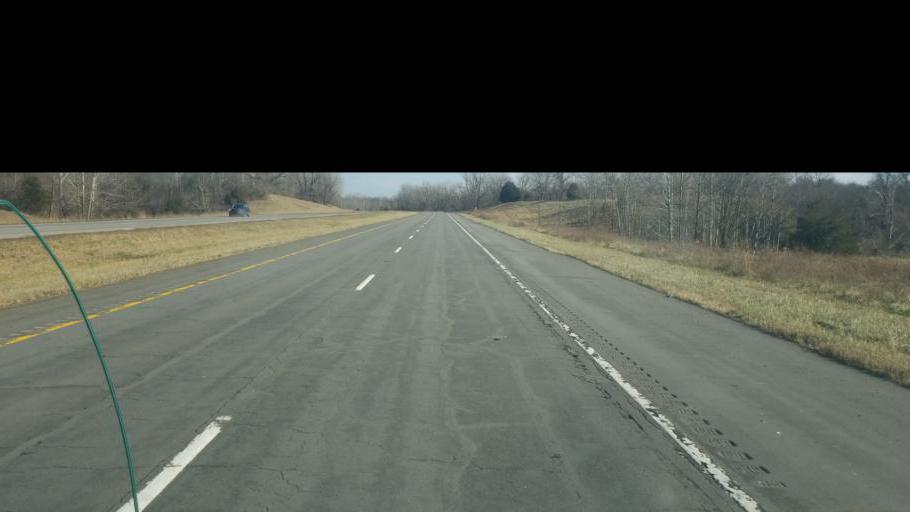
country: US
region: Illinois
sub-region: Saline County
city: Carrier Mills
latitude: 37.7306
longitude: -88.7395
